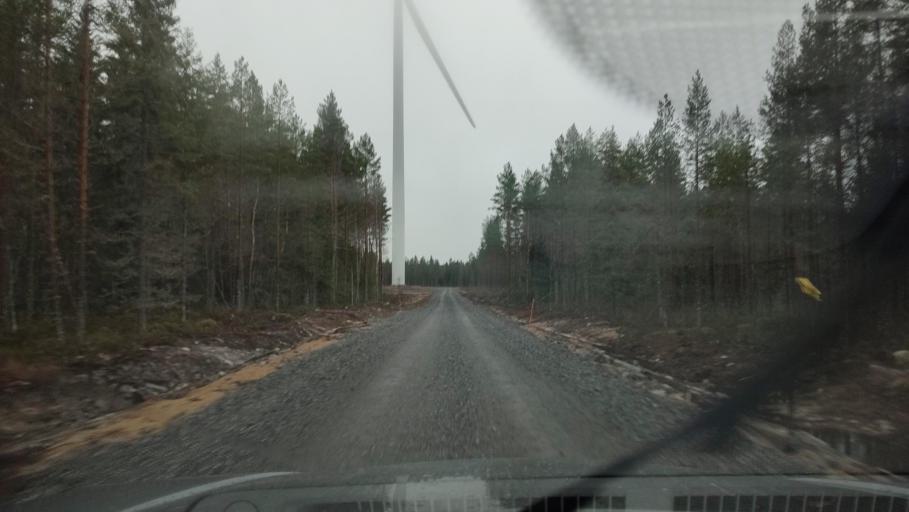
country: FI
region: Southern Ostrobothnia
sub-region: Suupohja
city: Karijoki
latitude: 62.1469
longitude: 21.6133
